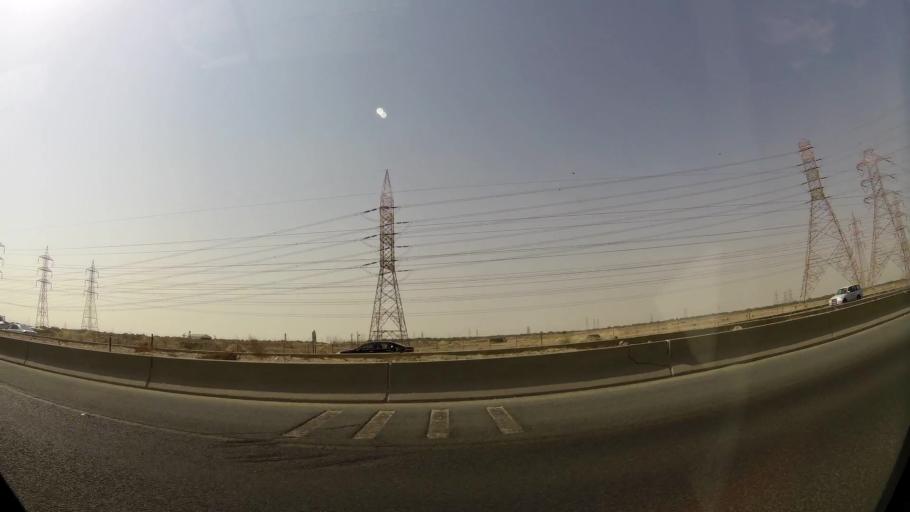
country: KW
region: Al Ahmadi
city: Al Ahmadi
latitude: 29.0557
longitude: 48.1095
